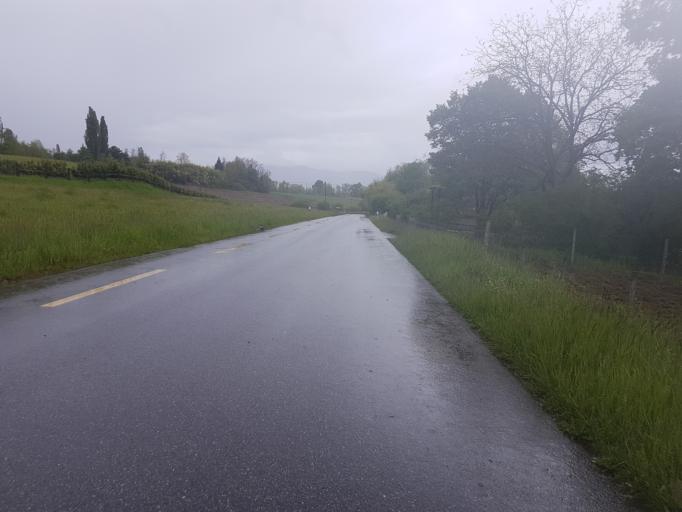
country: CH
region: Geneva
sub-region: Geneva
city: Chancy
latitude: 46.1601
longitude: 5.9878
